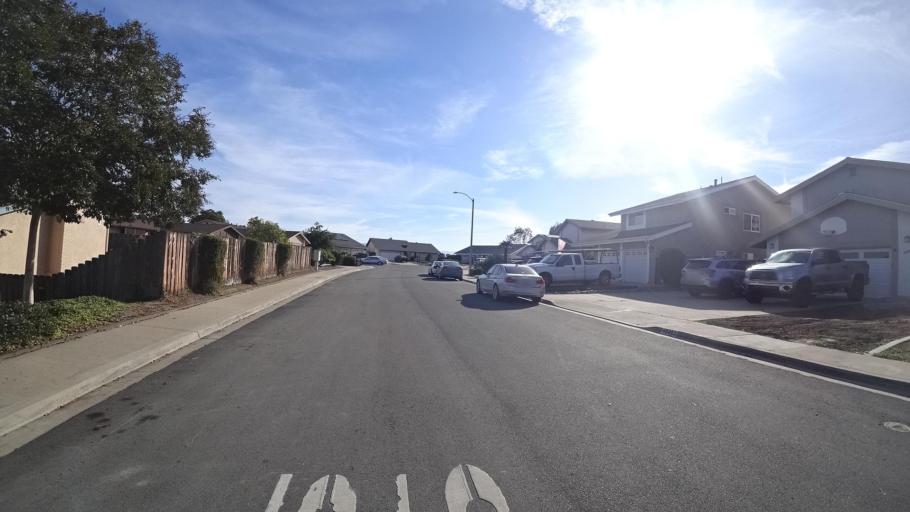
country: US
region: California
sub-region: San Diego County
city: Casa de Oro-Mount Helix
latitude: 32.7433
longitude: -116.9603
